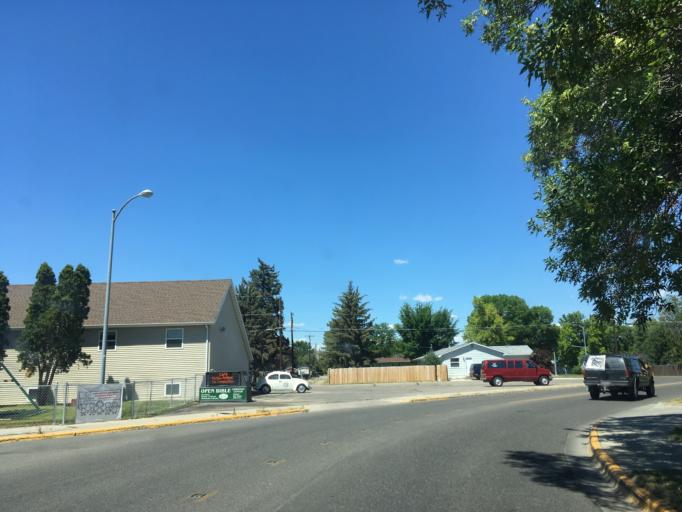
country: US
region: Montana
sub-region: Yellowstone County
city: Billings
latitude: 45.7727
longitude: -108.5647
